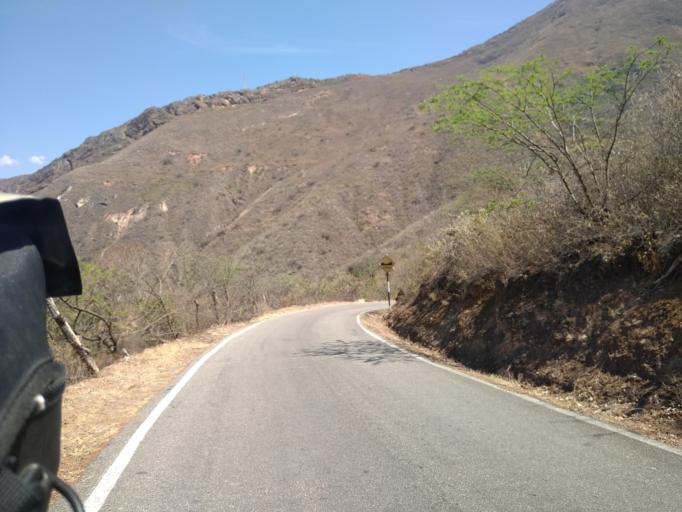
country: PE
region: Amazonas
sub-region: Provincia de Chachapoyas
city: Balsas
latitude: -6.8483
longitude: -77.9688
